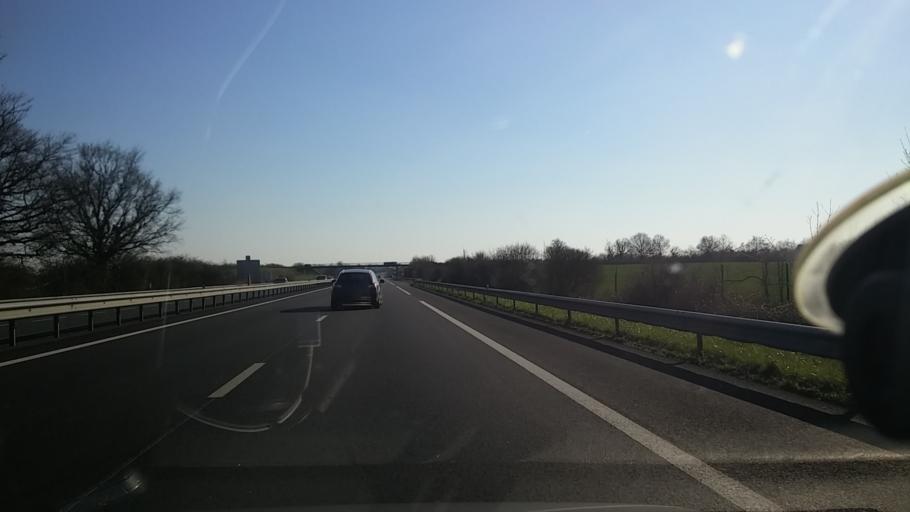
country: FR
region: Centre
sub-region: Departement de l'Indre
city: Luant
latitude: 46.7201
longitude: 1.5997
